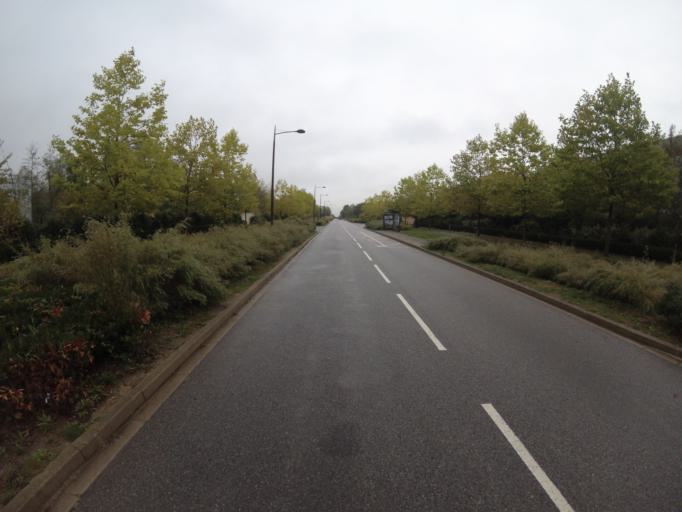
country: FR
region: Ile-de-France
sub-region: Departement de Seine-et-Marne
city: Bussy-Saint-Georges
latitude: 48.8340
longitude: 2.7009
